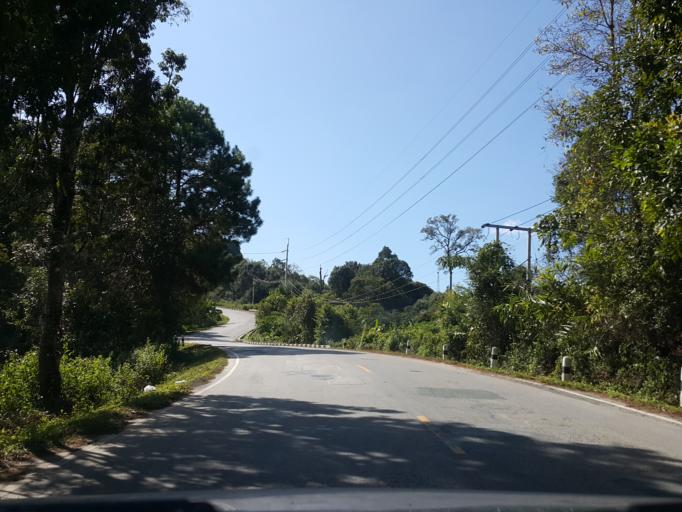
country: TH
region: Mae Hong Son
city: Mae Hi
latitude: 19.2698
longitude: 98.5956
